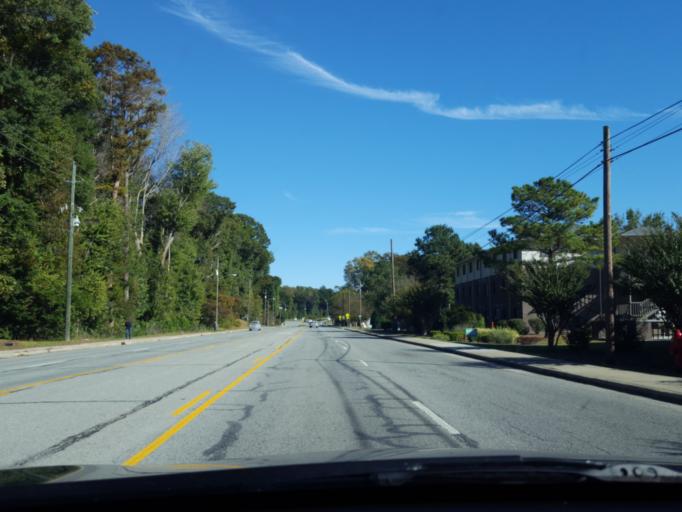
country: US
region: North Carolina
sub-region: Pitt County
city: Greenville
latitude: 35.6031
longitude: -77.3565
